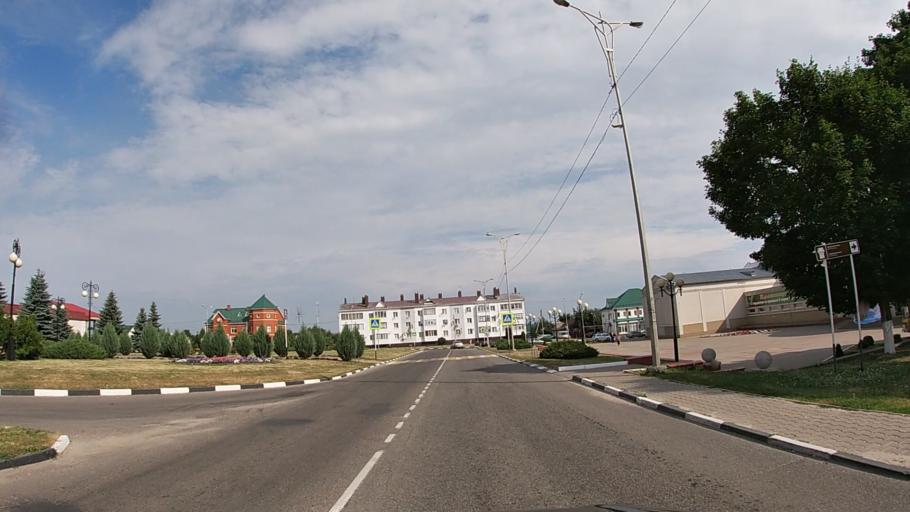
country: RU
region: Belgorod
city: Krasnaya Yaruga
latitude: 50.8018
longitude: 35.6599
